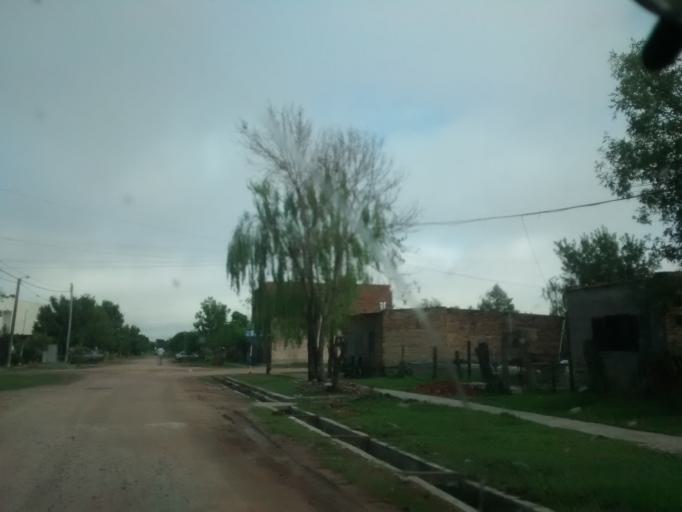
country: AR
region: Chaco
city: Fontana
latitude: -27.4573
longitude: -59.0298
